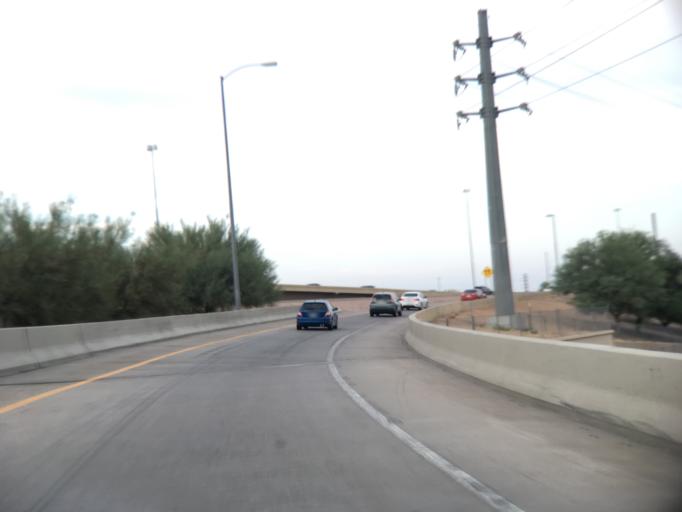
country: US
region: Arizona
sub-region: Maricopa County
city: Guadalupe
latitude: 33.3870
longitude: -111.9659
